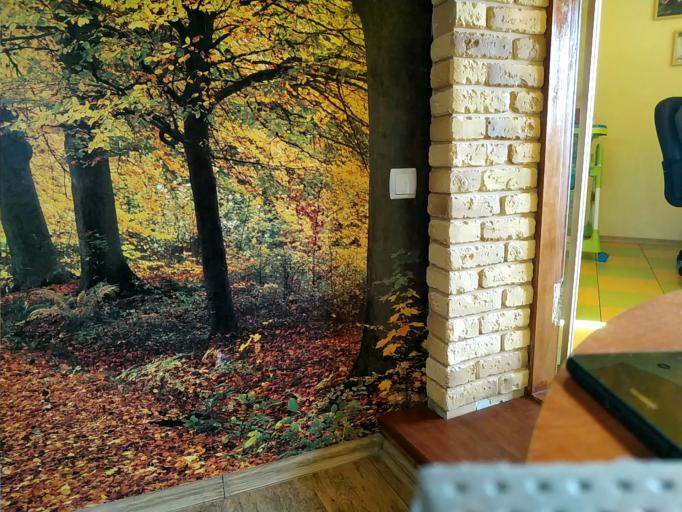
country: RU
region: Tverskaya
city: Zubtsov
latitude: 56.2070
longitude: 34.5868
